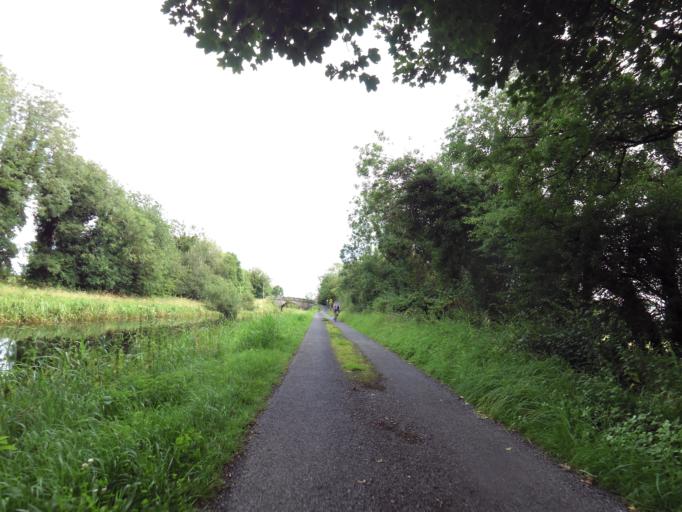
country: IE
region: Leinster
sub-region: An Iarmhi
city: An Muileann gCearr
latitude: 53.5576
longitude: -7.4844
